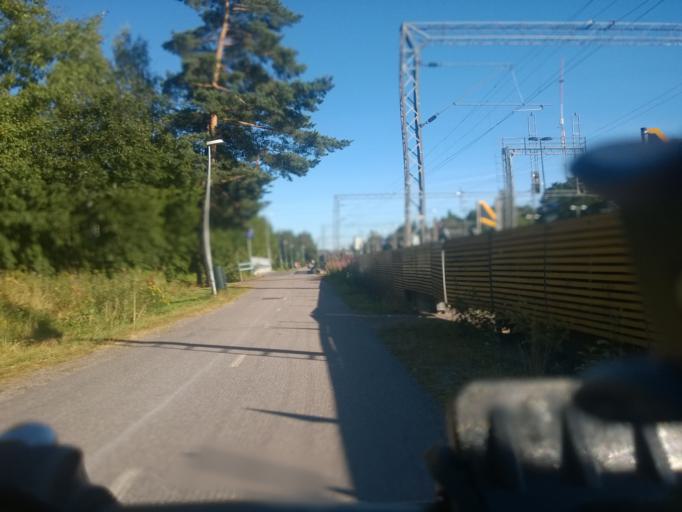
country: FI
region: Uusimaa
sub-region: Helsinki
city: Teekkarikylae
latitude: 60.2198
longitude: 24.8900
